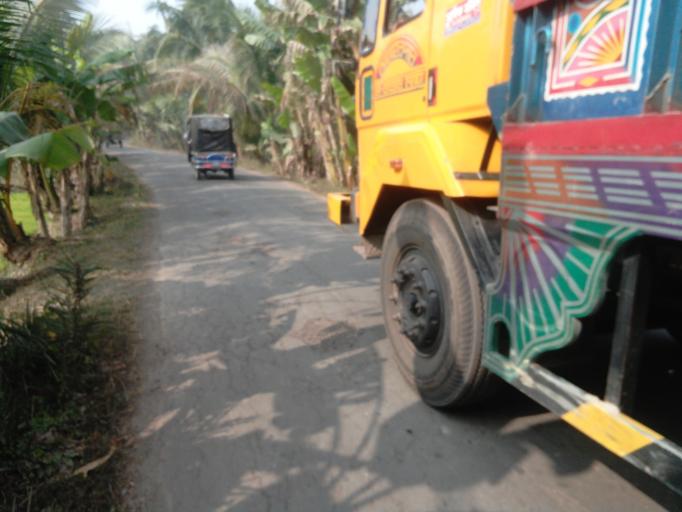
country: BD
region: Khulna
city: Kesabpur
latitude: 22.7500
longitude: 89.2425
